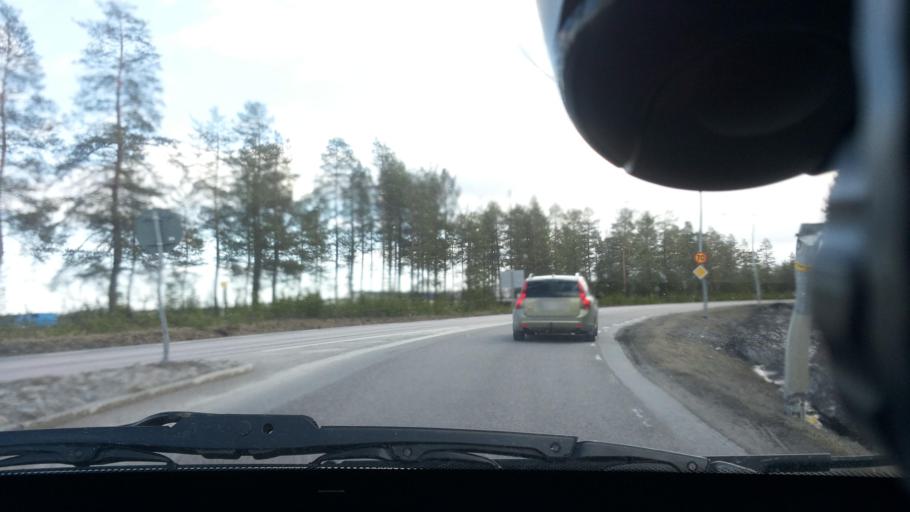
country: SE
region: Norrbotten
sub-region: Lulea Kommun
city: Gammelstad
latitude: 65.6148
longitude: 22.0427
